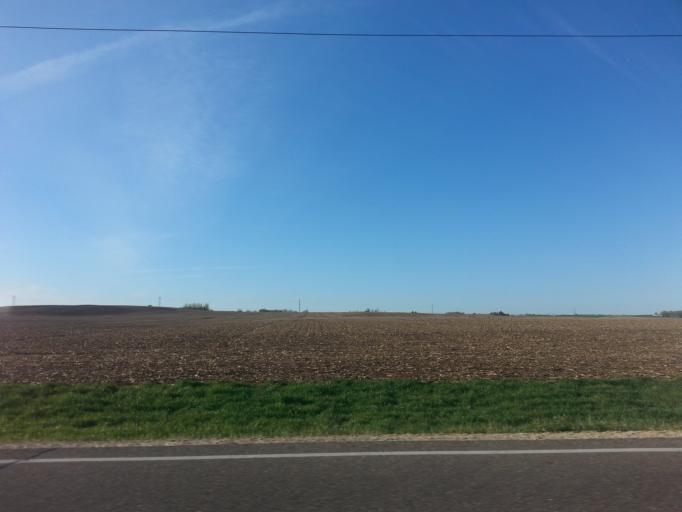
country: US
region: Minnesota
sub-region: Goodhue County
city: Cannon Falls
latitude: 44.5435
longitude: -93.0327
